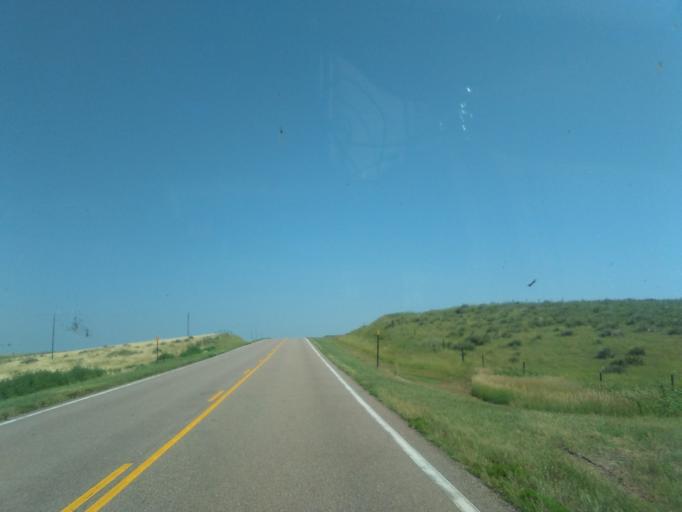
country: US
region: Nebraska
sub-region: Dundy County
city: Benkelman
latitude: 39.9368
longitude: -101.5413
